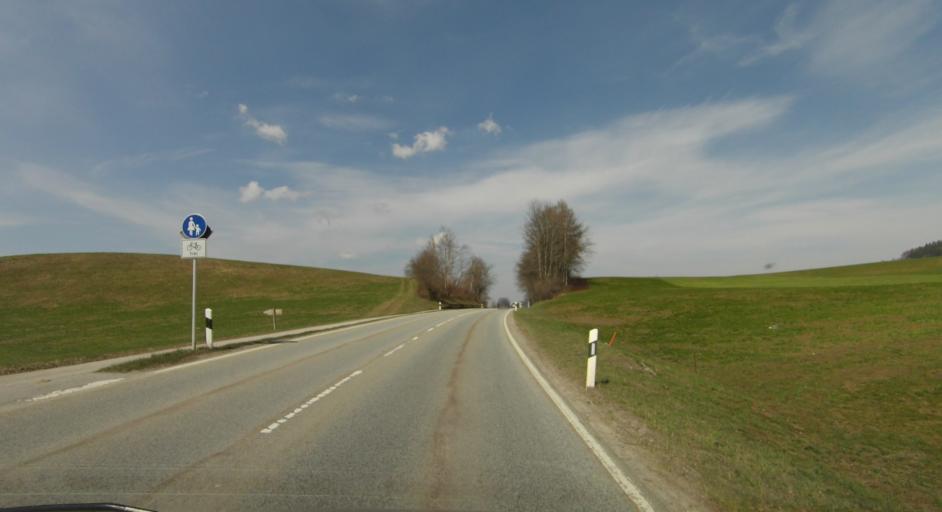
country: DE
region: Bavaria
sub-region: Upper Bavaria
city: Schliersee
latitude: 47.7403
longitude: 11.8507
